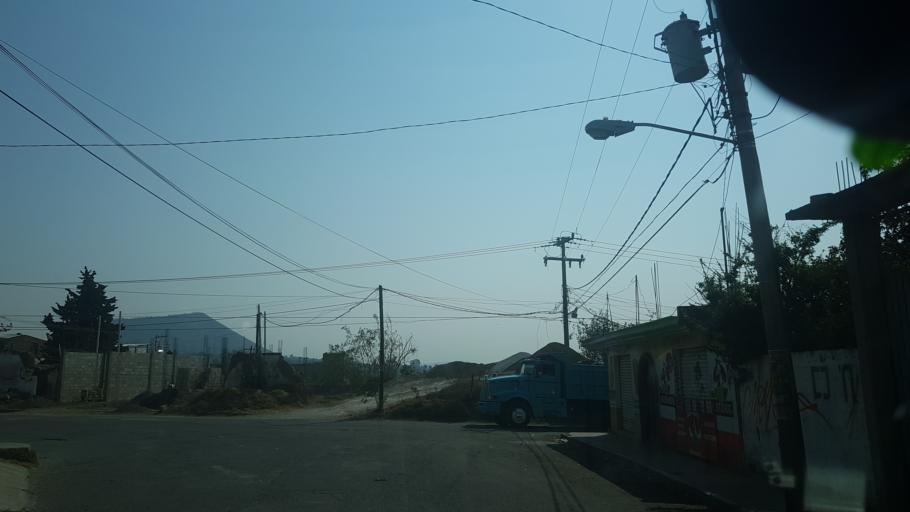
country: MX
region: Puebla
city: Nealtican
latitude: 19.0510
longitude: -98.4216
